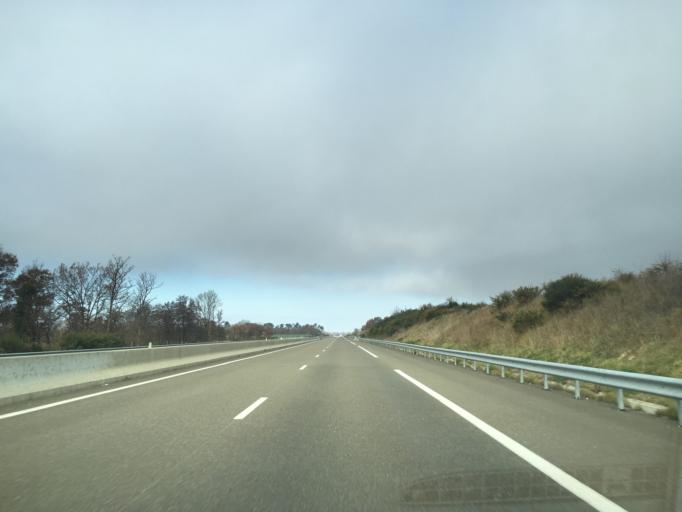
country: FR
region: Aquitaine
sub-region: Departement des Landes
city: Villeneuve-de-Marsan
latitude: 43.8340
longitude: -0.3231
